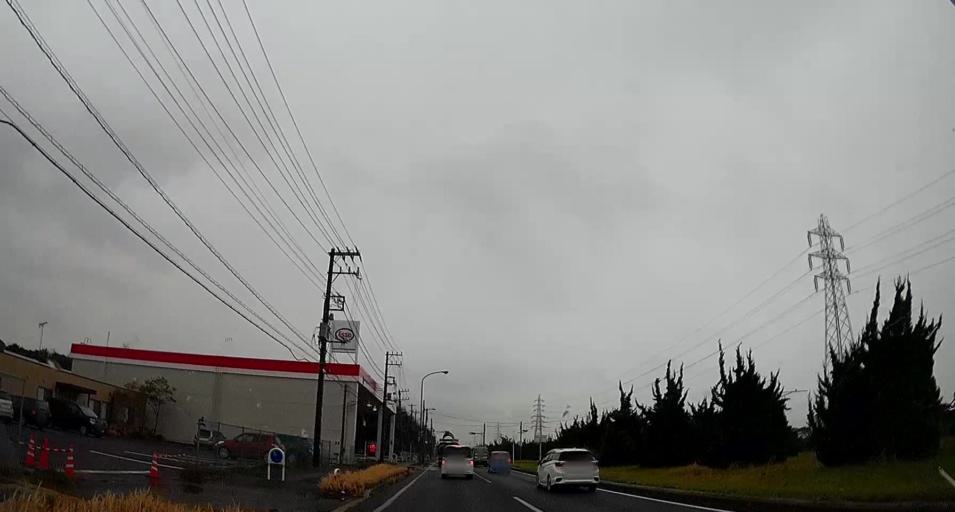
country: JP
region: Chiba
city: Ichihara
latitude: 35.5128
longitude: 140.0570
